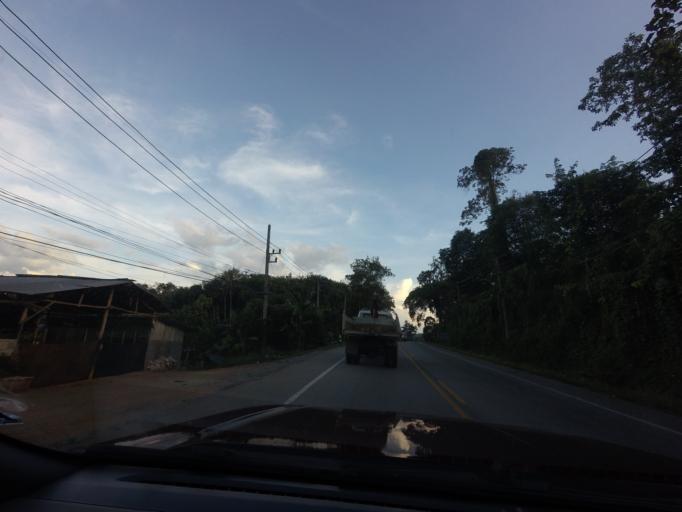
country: TH
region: Yala
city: Than To
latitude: 6.1252
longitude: 101.1922
